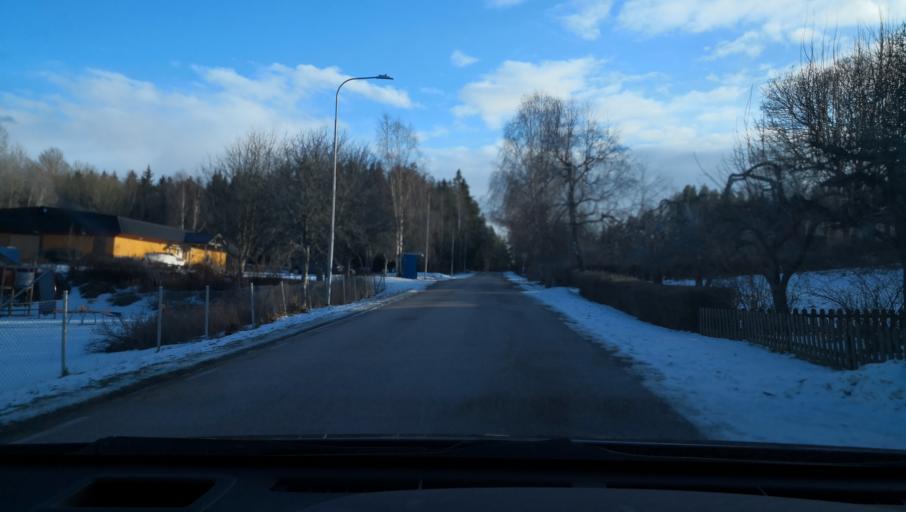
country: SE
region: Uppsala
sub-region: Enkopings Kommun
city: Irsta
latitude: 59.6763
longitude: 16.8381
